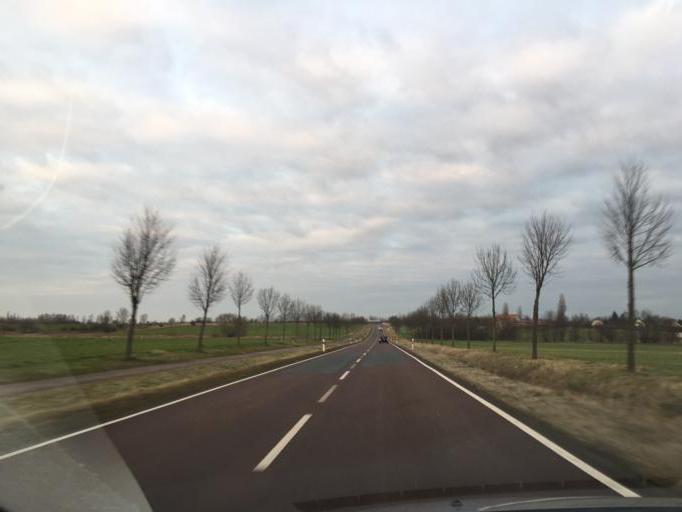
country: DE
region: Saxony
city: Espenhain
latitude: 51.2183
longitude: 12.4577
